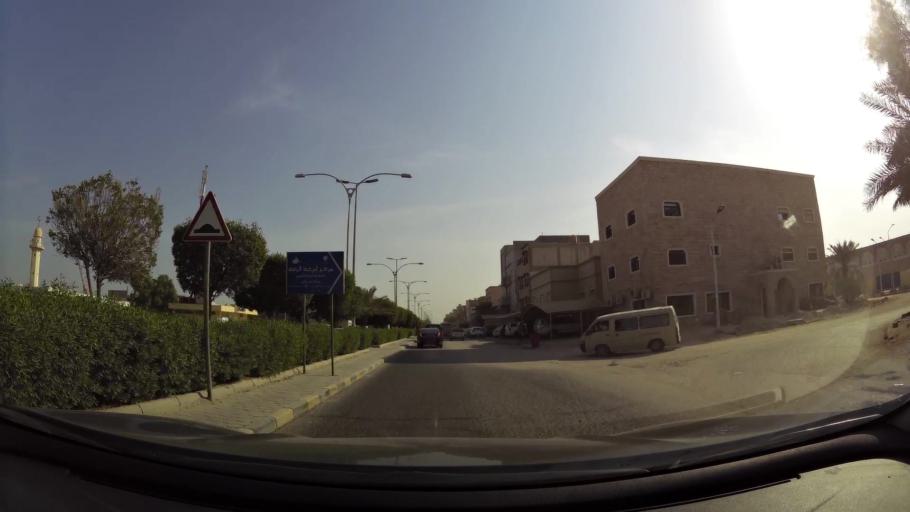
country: KW
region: Al Ahmadi
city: Ar Riqqah
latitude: 29.1551
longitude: 48.1041
